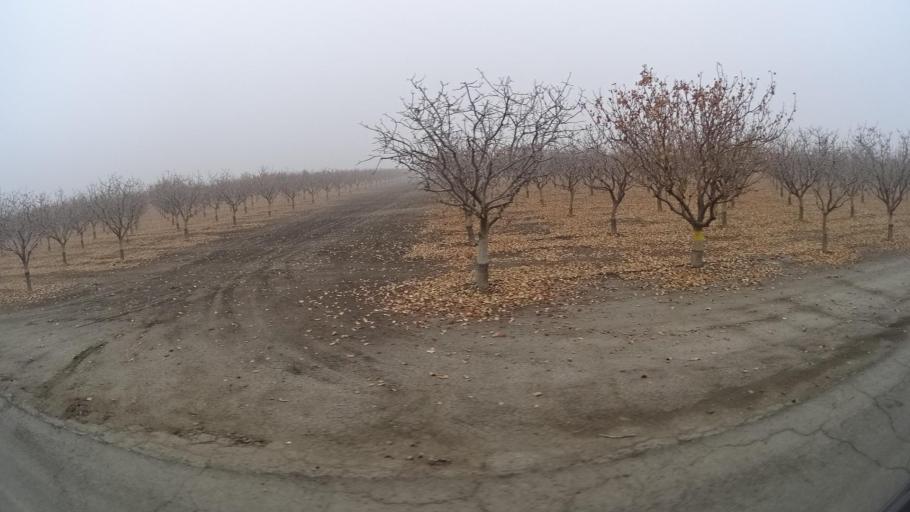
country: US
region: California
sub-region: Kern County
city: Buttonwillow
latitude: 35.4124
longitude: -119.5412
